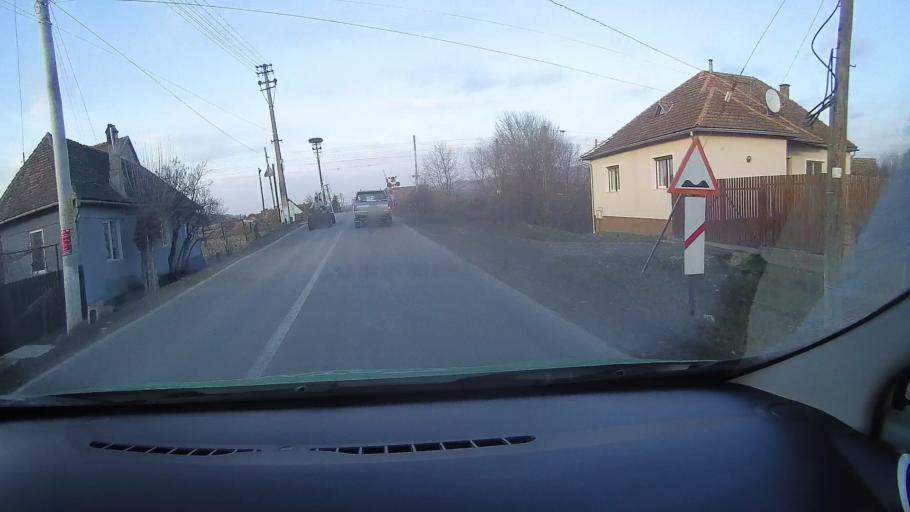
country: RO
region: Mures
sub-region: Comuna Vanatori
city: Vanatori
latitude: 46.2427
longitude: 24.9229
